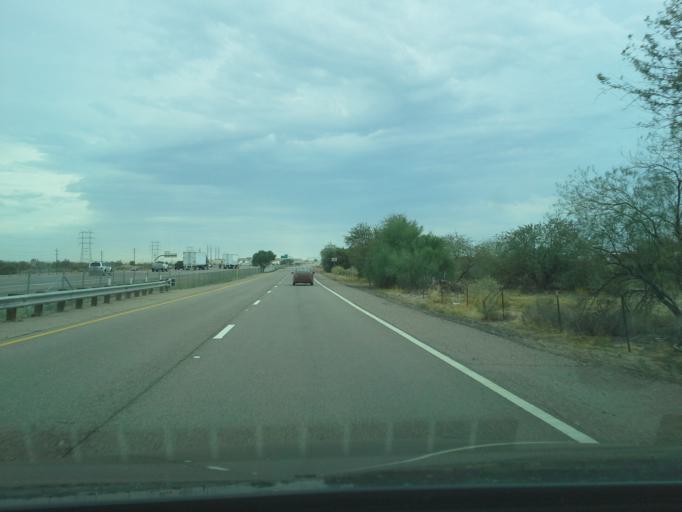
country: US
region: Arizona
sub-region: Pima County
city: Tortolita
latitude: 32.3897
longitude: -111.1187
